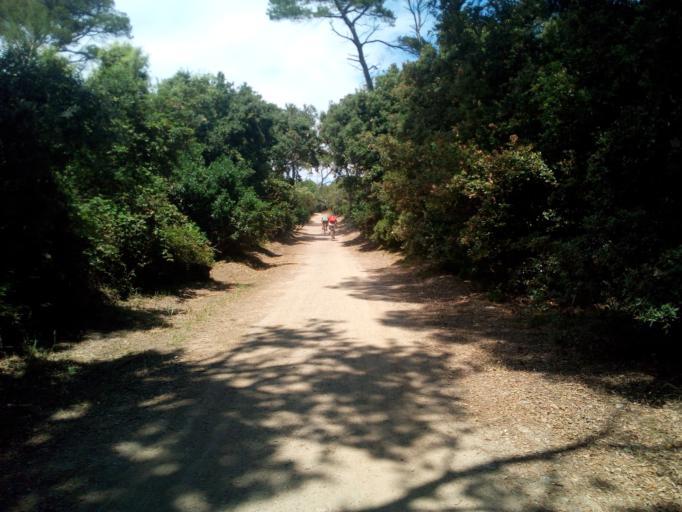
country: FR
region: Provence-Alpes-Cote d'Azur
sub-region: Departement du Var
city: La Londe-les-Maures
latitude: 43.0123
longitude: 6.2358
